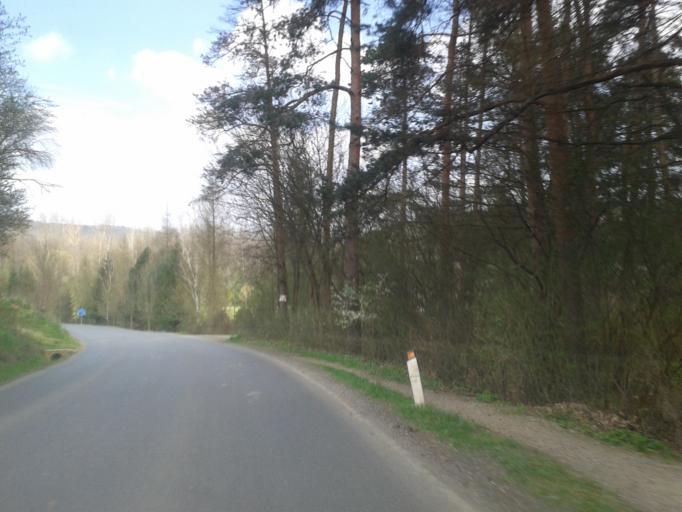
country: CZ
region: Central Bohemia
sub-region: Okres Beroun
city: Lodenice
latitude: 50.0091
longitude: 14.1510
